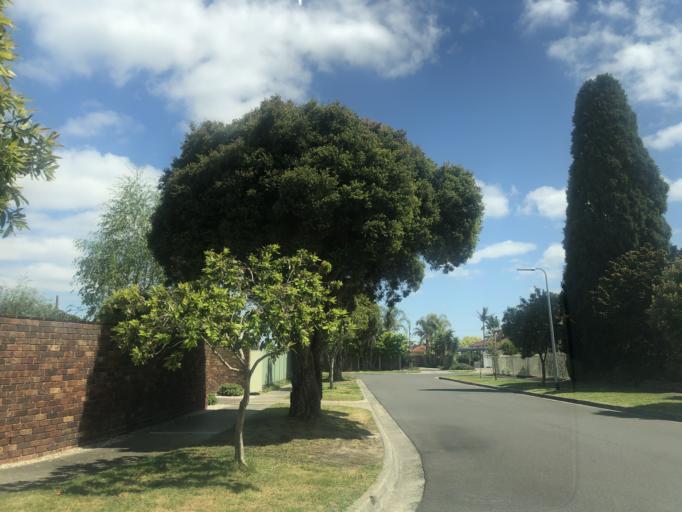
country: AU
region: Victoria
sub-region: Monash
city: Mulgrave
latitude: -37.9196
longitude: 145.1847
